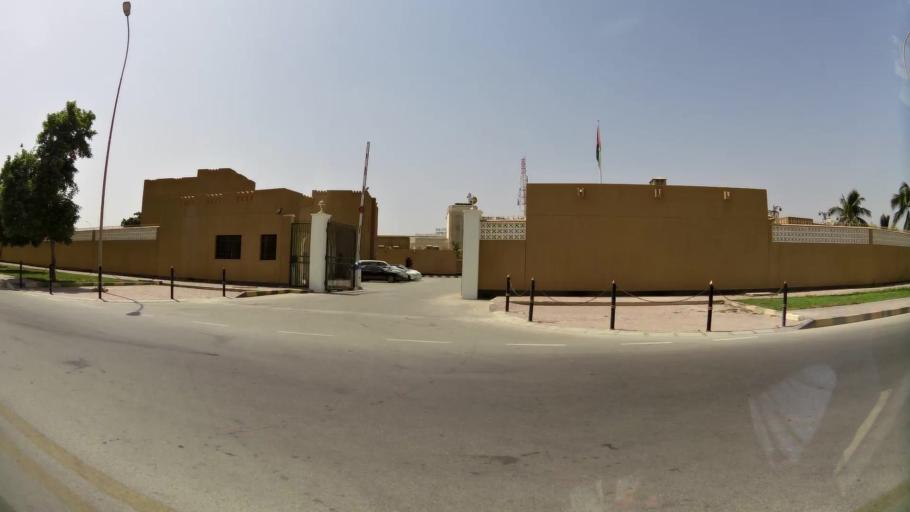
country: OM
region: Zufar
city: Salalah
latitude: 17.0174
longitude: 54.0918
